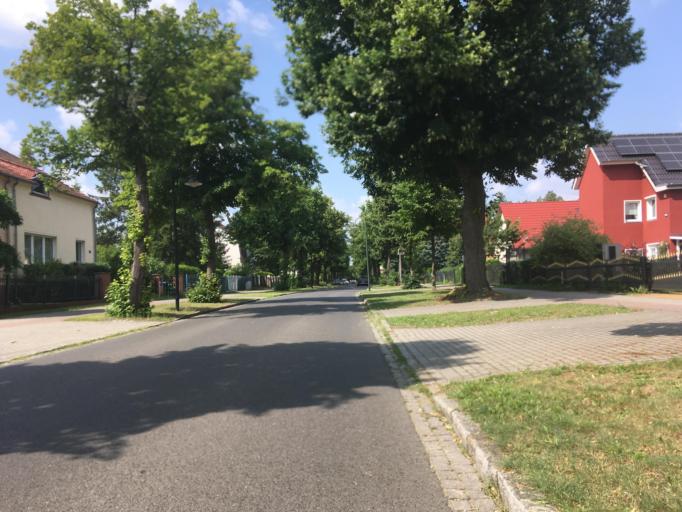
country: DE
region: Brandenburg
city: Zeuthen
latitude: 52.3586
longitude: 13.6254
